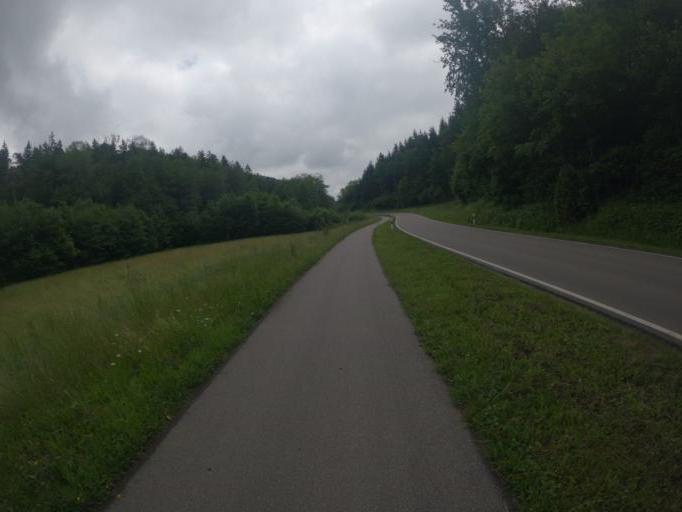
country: DE
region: Baden-Wuerttemberg
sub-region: Regierungsbezirk Stuttgart
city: Ebersbach an der Fils
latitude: 48.7331
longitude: 9.5521
